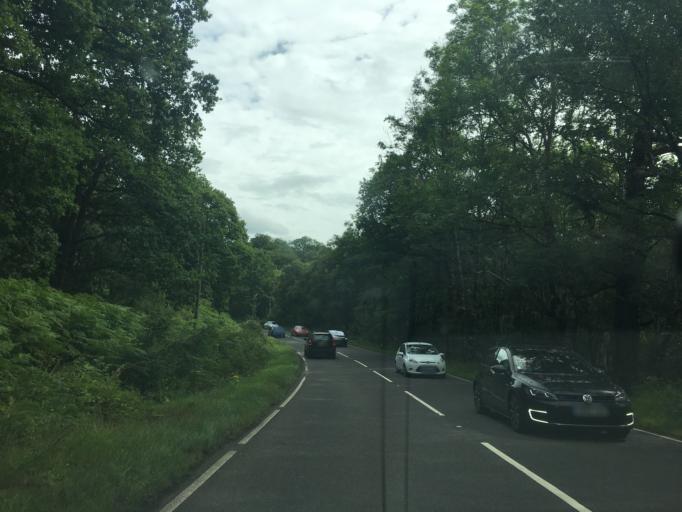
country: GB
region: Scotland
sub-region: Stirling
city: Callander
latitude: 56.2503
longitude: -4.2780
